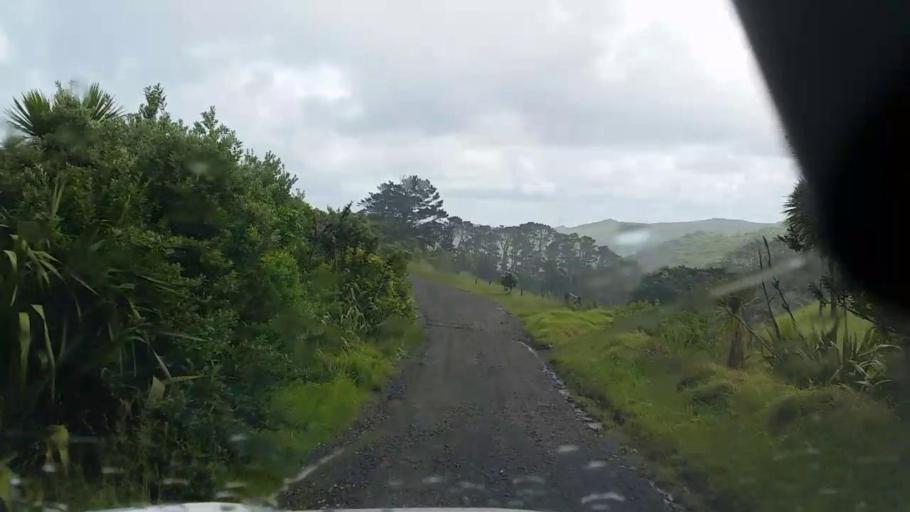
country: NZ
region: Auckland
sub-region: Auckland
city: Muriwai Beach
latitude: -36.9272
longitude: 174.4593
